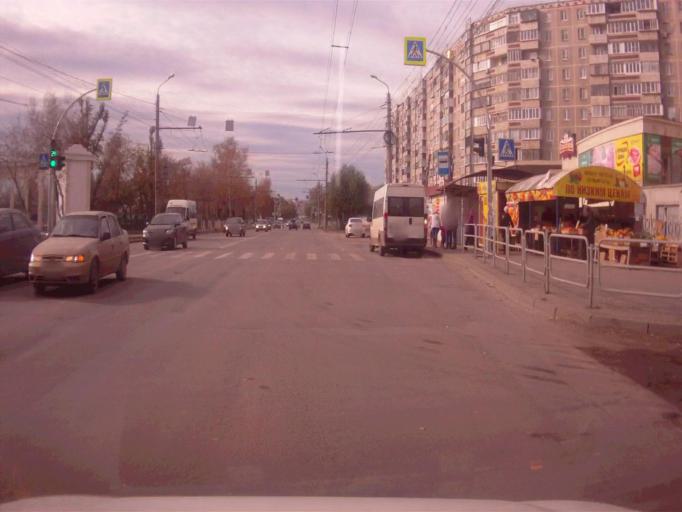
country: RU
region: Chelyabinsk
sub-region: Gorod Chelyabinsk
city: Chelyabinsk
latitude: 55.1136
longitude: 61.4579
